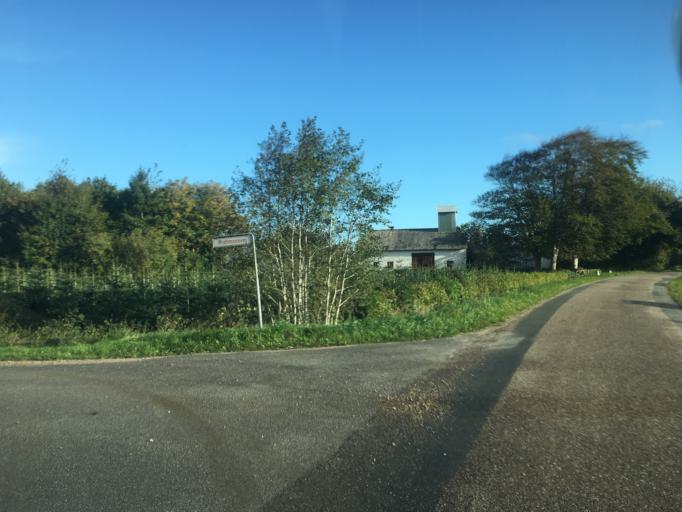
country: DE
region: Schleswig-Holstein
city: Ellhoft
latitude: 54.9621
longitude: 8.9870
